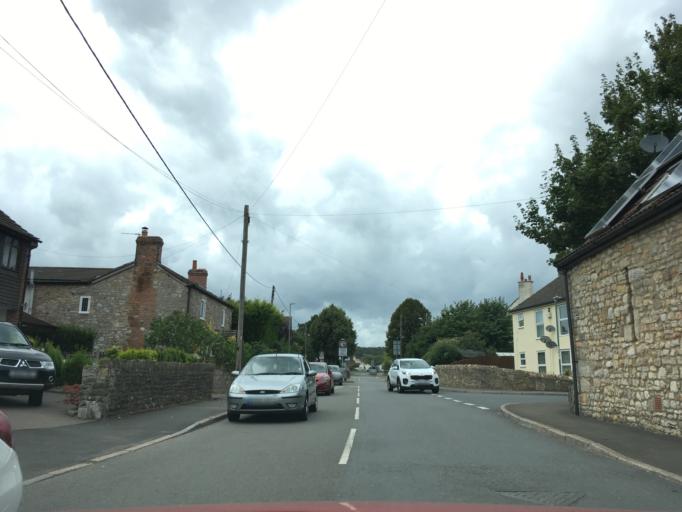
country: GB
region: Wales
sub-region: Monmouthshire
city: Chepstow
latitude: 51.6204
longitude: -2.6946
